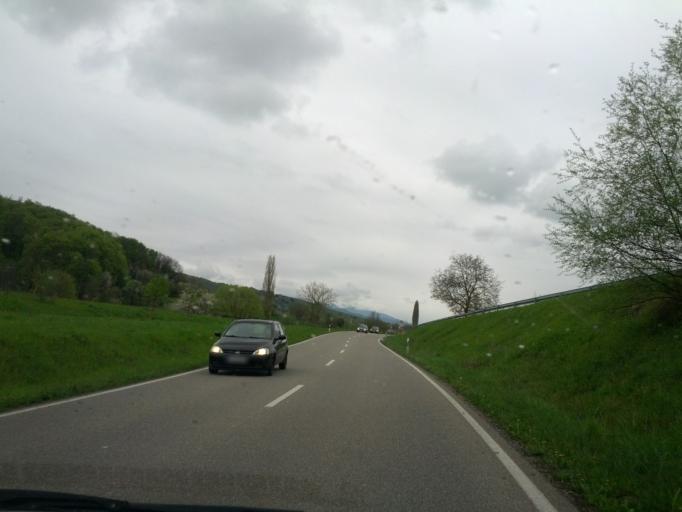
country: DE
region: Baden-Wuerttemberg
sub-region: Freiburg Region
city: Schallstadt
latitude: 47.9521
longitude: 7.7605
